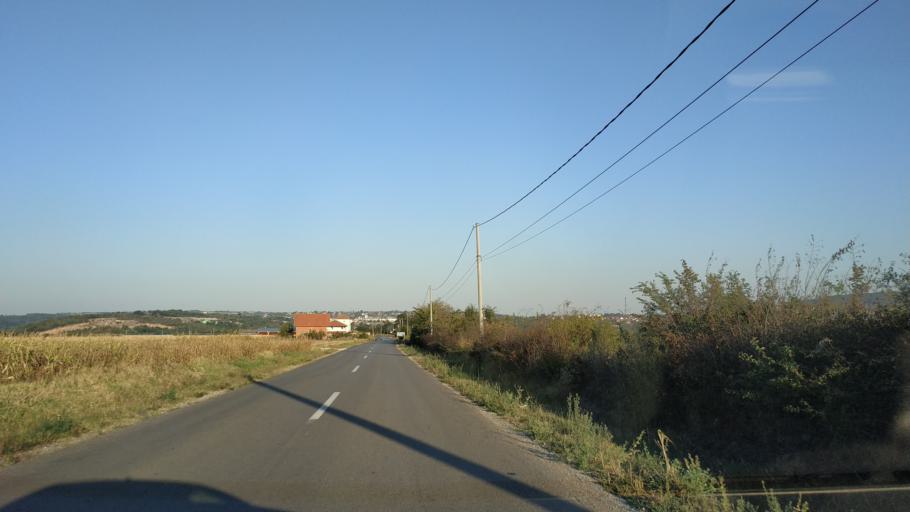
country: RS
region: Central Serbia
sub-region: Sumadijski Okrug
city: Topola
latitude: 44.2681
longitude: 20.6584
